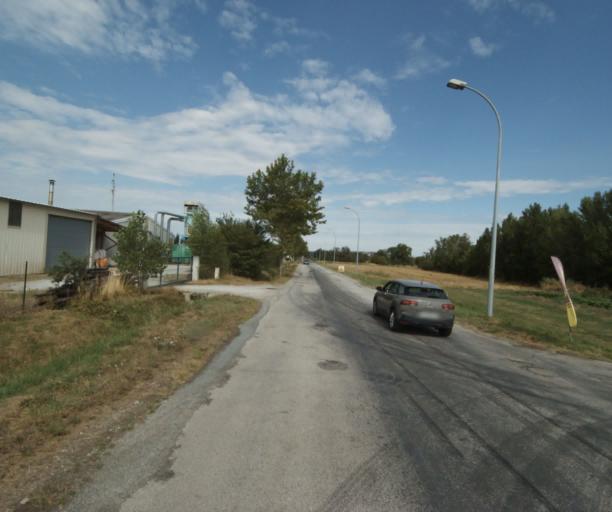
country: FR
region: Midi-Pyrenees
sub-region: Departement de la Haute-Garonne
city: Revel
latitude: 43.4550
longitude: 1.9870
